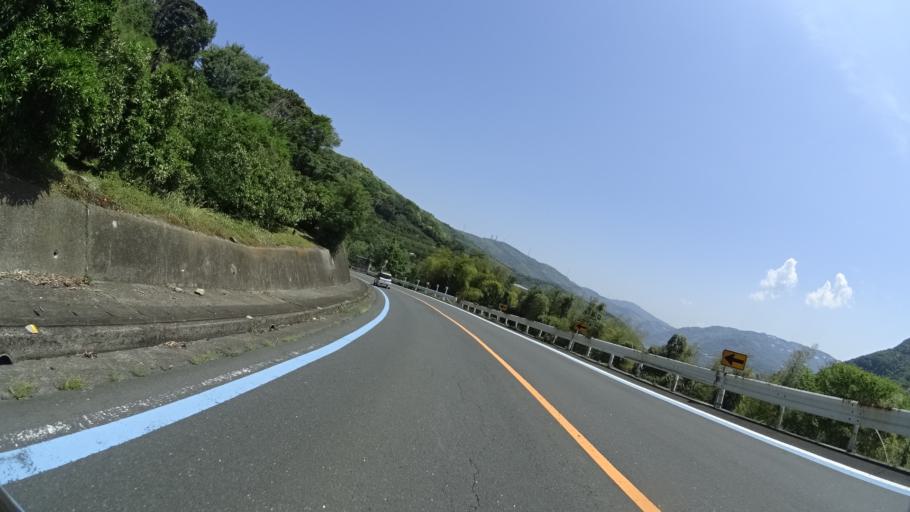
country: JP
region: Ehime
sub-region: Nishiuwa-gun
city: Ikata-cho
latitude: 33.4832
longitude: 132.3343
